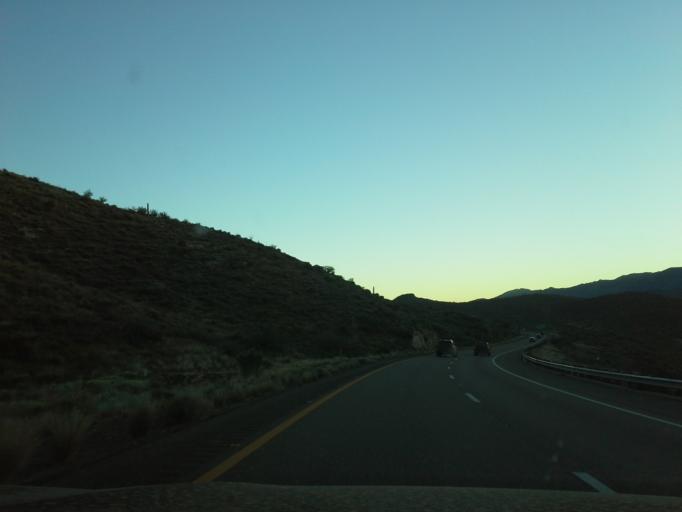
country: US
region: Arizona
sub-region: Yavapai County
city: Black Canyon City
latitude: 34.1536
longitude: -112.1466
